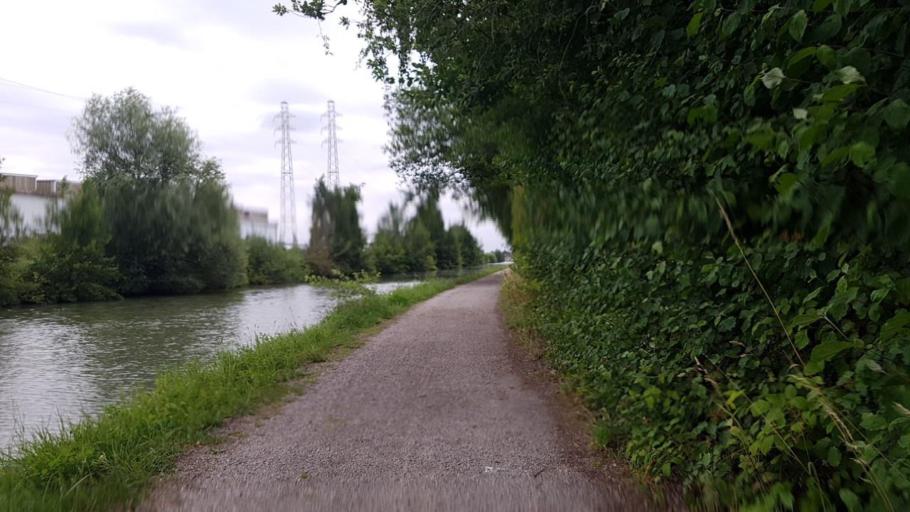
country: FR
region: Picardie
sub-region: Departement de l'Aisne
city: Beautor
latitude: 49.6530
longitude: 3.3309
